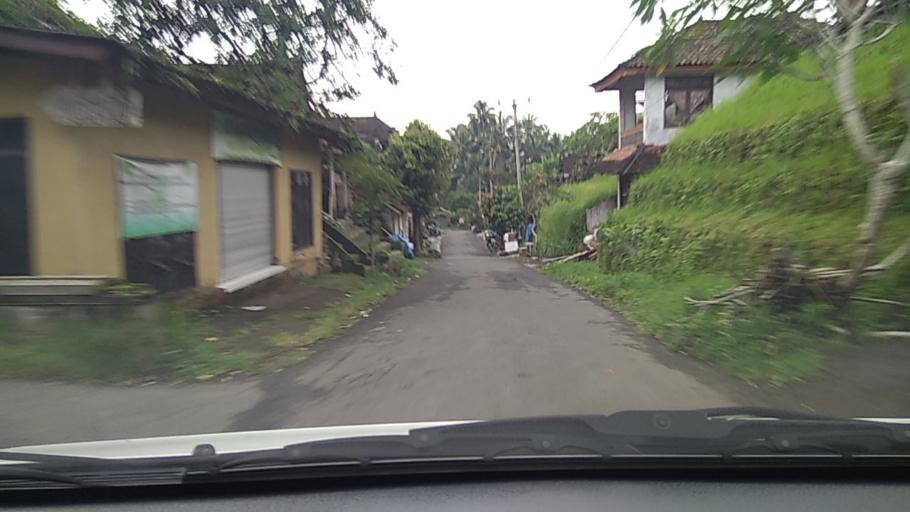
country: ID
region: Bali
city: Banjar Dujung Kaja
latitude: -8.4176
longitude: 115.2822
